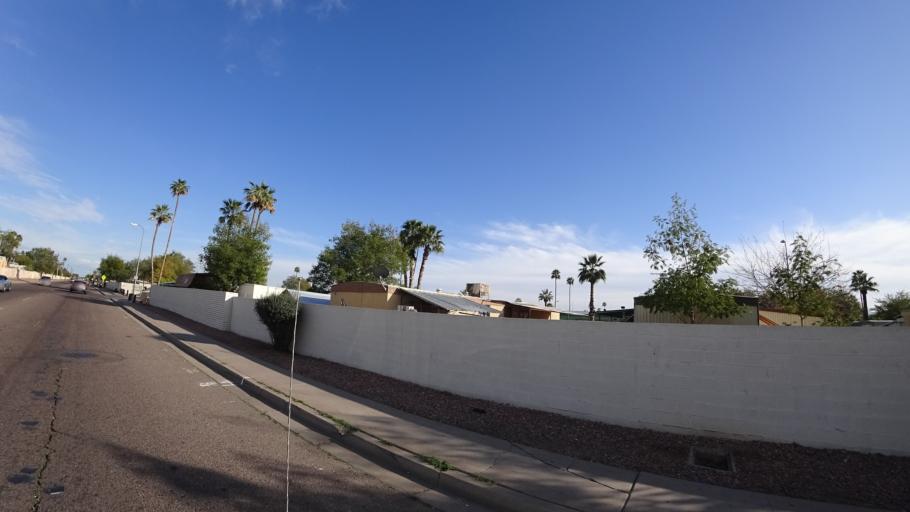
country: US
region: Arizona
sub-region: Maricopa County
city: Phoenix
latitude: 33.4586
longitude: -112.1500
